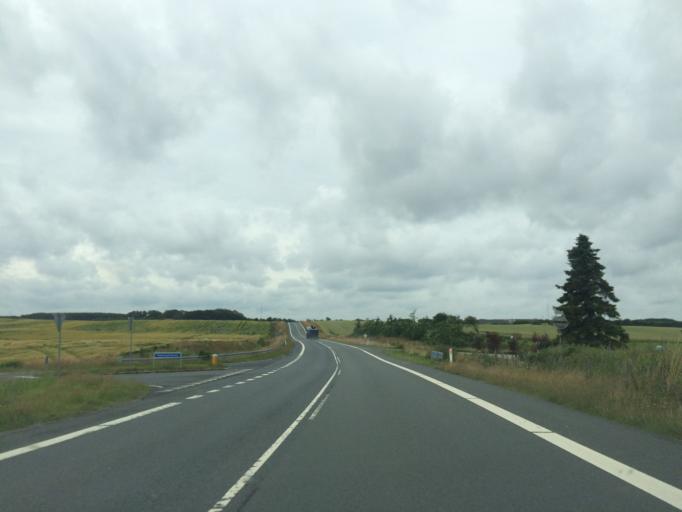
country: DK
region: Central Jutland
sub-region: Silkeborg Kommune
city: Silkeborg
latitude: 56.2114
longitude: 9.6090
